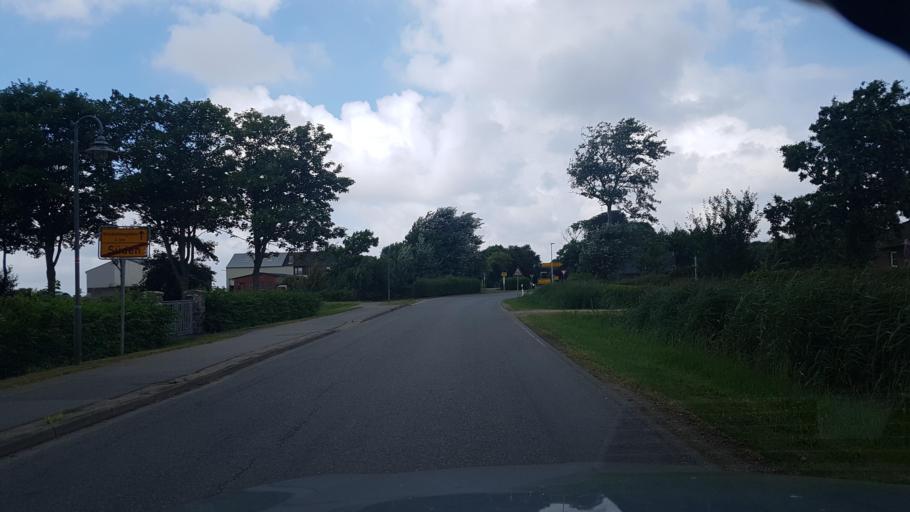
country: DE
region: Schleswig-Holstein
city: Elisabeth-Sophien-Koog
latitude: 54.4876
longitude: 8.8492
